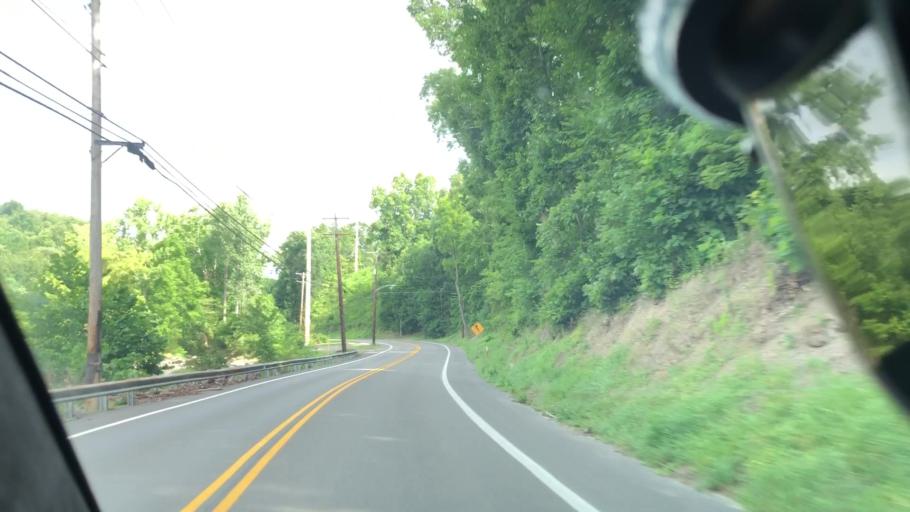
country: US
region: Pennsylvania
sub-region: Allegheny County
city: Upper Saint Clair
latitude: 40.3504
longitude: -80.0848
